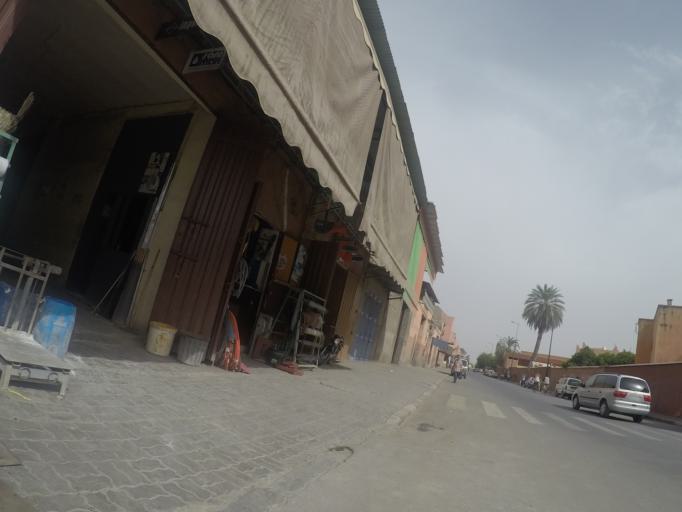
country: MA
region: Marrakech-Tensift-Al Haouz
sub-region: Marrakech
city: Marrakesh
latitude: 31.6191
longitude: -7.9756
